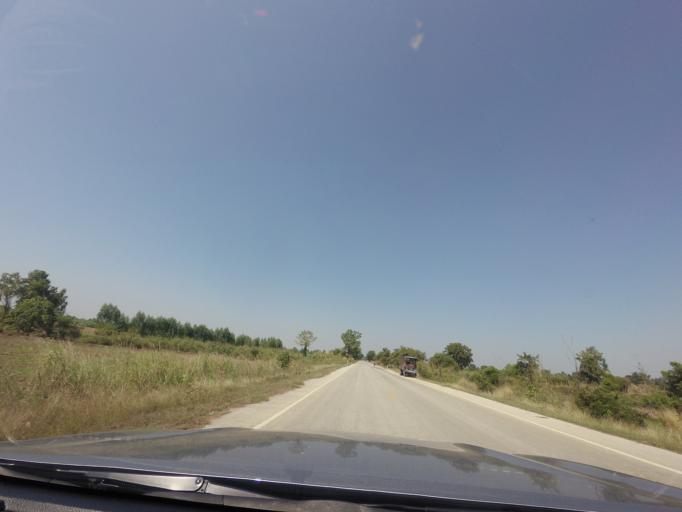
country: TH
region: Sukhothai
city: Sukhothai
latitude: 17.0915
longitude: 99.7895
